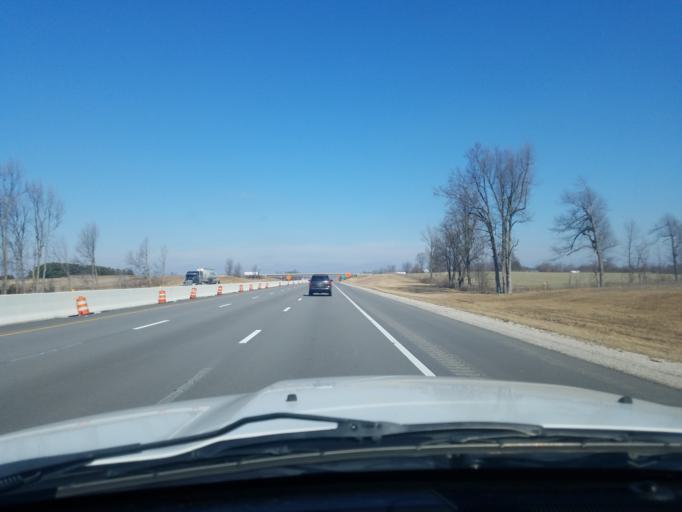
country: US
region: Kentucky
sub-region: Larue County
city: Hodgenville
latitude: 37.5346
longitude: -85.8818
